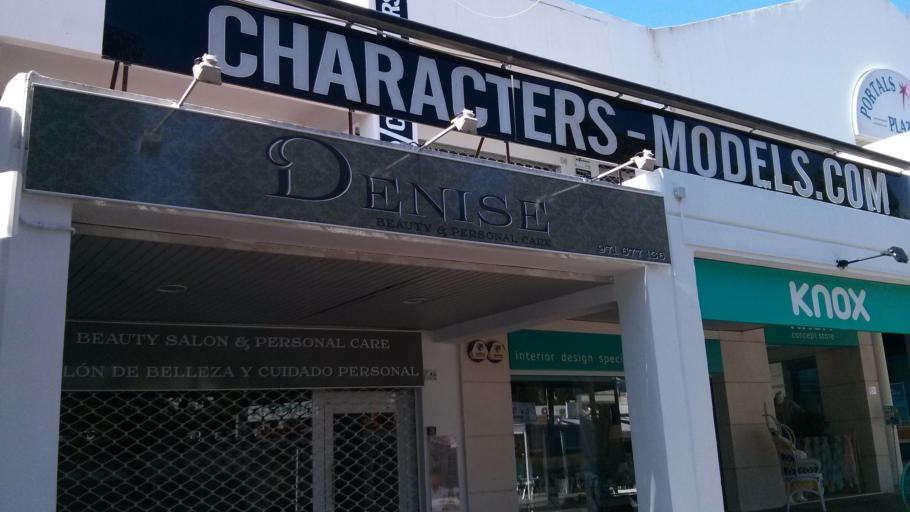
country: ES
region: Balearic Islands
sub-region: Illes Balears
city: Magaluf
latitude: 39.5353
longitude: 2.5713
